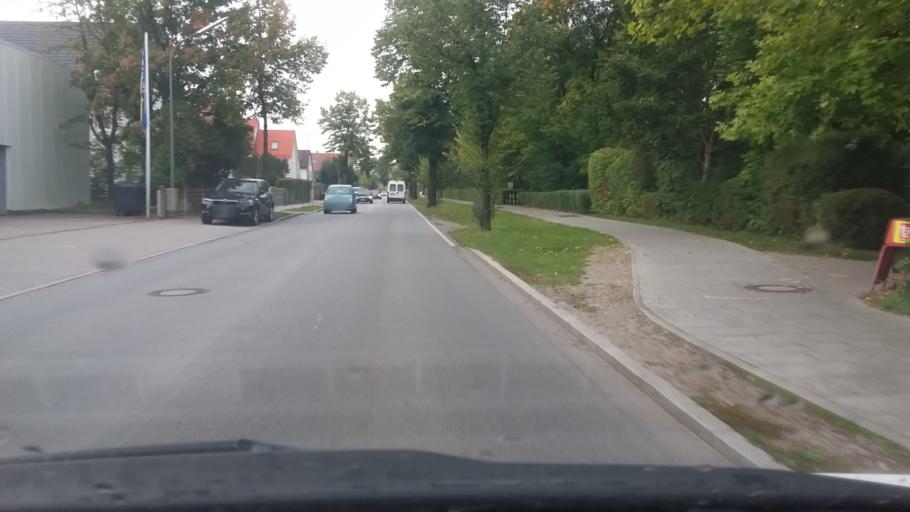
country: DE
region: Bavaria
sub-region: Upper Bavaria
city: Oberschleissheim
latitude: 48.2562
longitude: 11.5565
